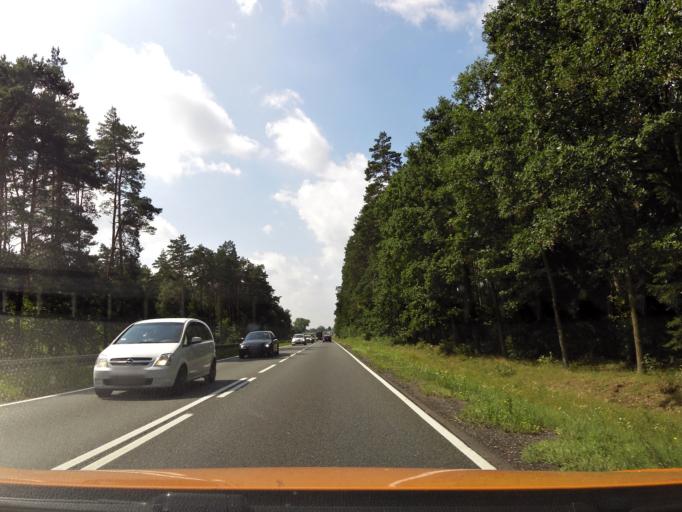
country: PL
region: West Pomeranian Voivodeship
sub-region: Powiat goleniowski
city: Nowogard
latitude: 53.6963
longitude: 15.1595
